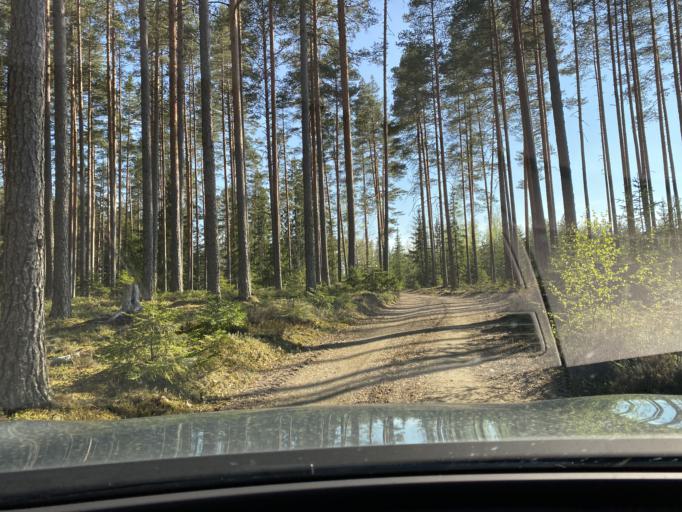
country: FI
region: Pirkanmaa
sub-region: Lounais-Pirkanmaa
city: Punkalaidun
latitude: 61.0139
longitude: 23.2044
